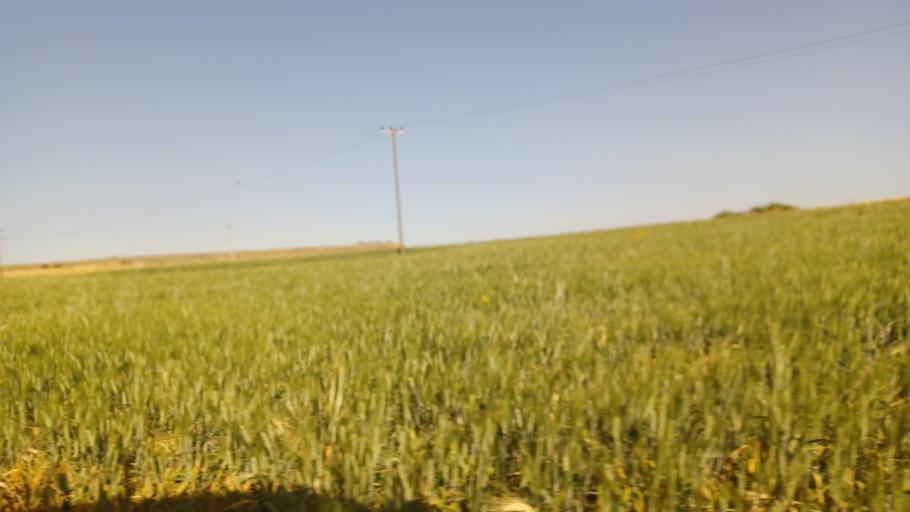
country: CY
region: Lefkosia
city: Mammari
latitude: 35.1634
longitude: 33.2463
